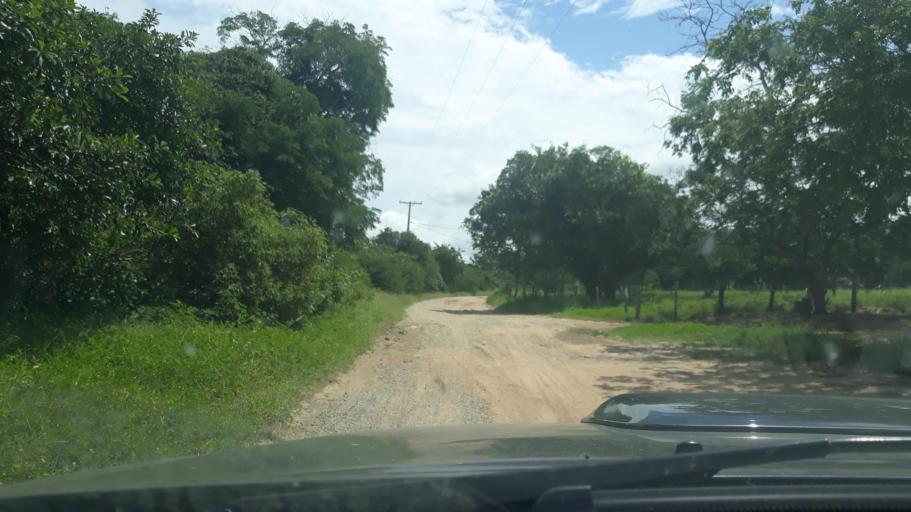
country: BR
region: Bahia
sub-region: Riacho De Santana
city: Riacho de Santana
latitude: -13.8876
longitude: -43.0241
